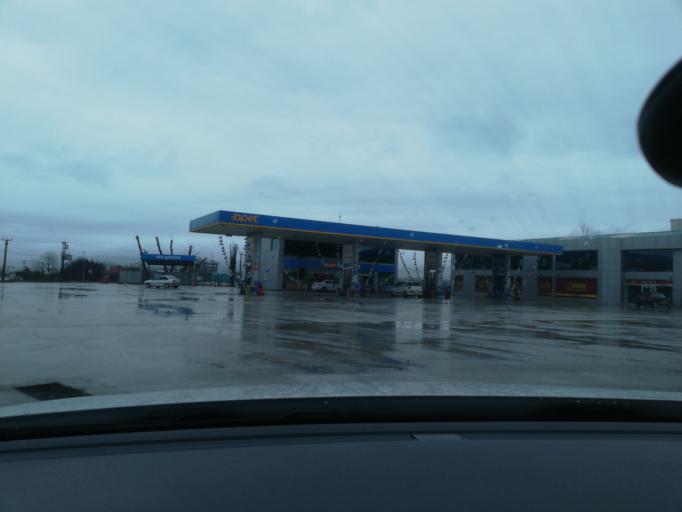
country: TR
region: Bolu
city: Bolu
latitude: 40.7372
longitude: 31.6569
